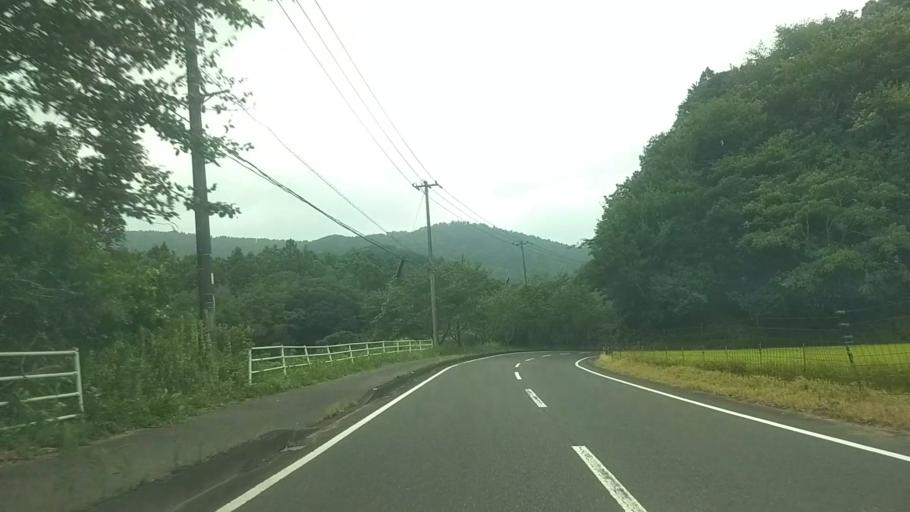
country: JP
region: Chiba
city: Kawaguchi
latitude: 35.2504
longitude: 140.0391
